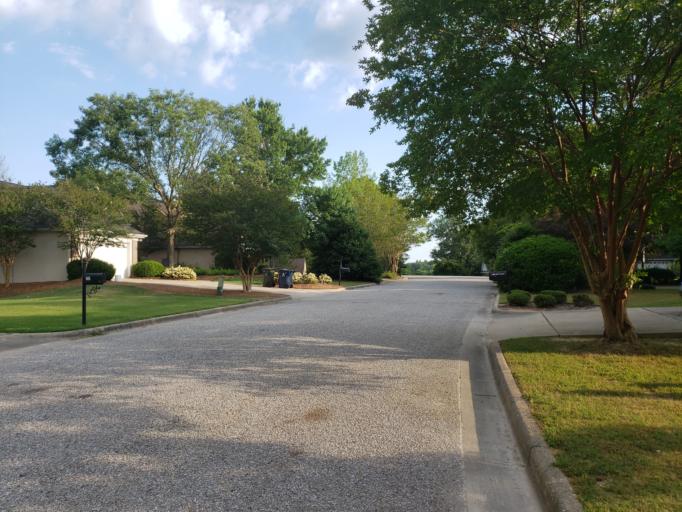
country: US
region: Alabama
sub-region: Lee County
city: Auburn
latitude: 32.5854
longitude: -85.4574
